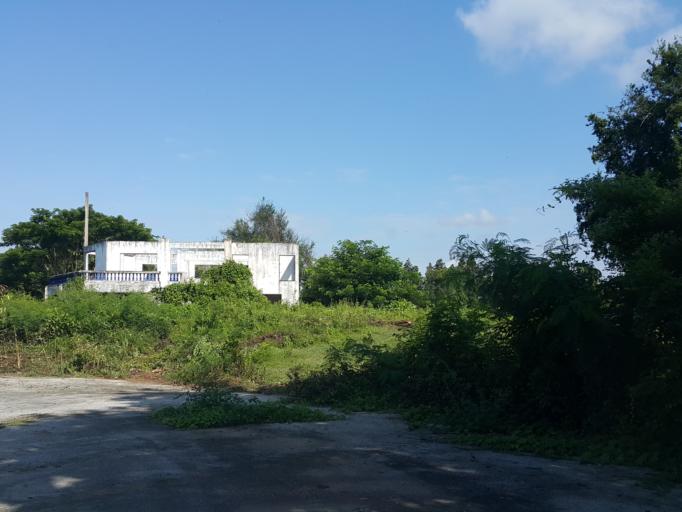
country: TH
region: Chiang Mai
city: Mae On
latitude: 18.8049
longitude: 99.1856
